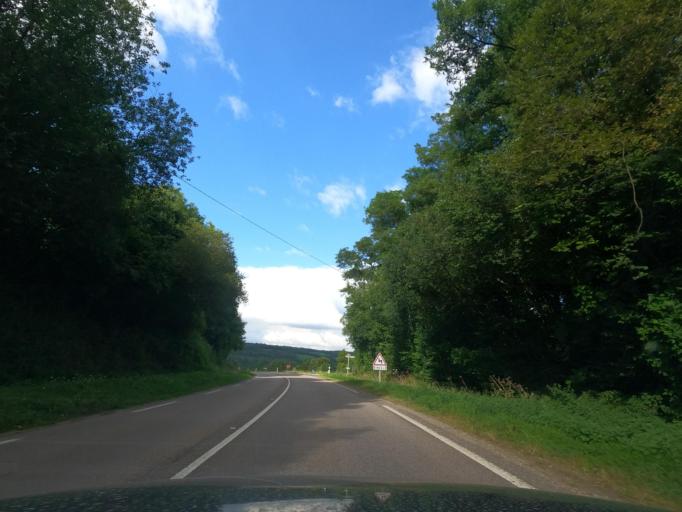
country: FR
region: Lower Normandy
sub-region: Departement de l'Orne
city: Gace
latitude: 48.8024
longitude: 0.3107
